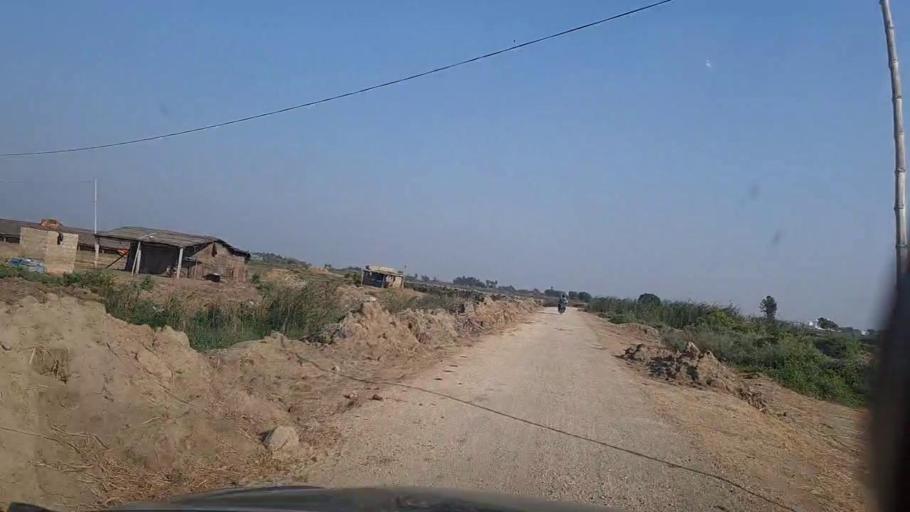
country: PK
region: Sindh
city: Thatta
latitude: 24.5860
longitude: 67.8783
